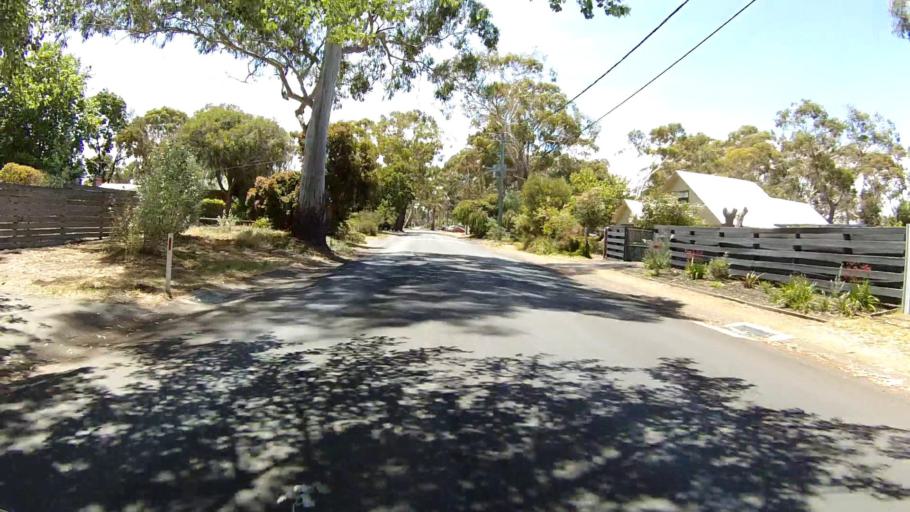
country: AU
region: Tasmania
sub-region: Clarence
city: Seven Mile Beach
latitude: -42.8608
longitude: 147.5054
